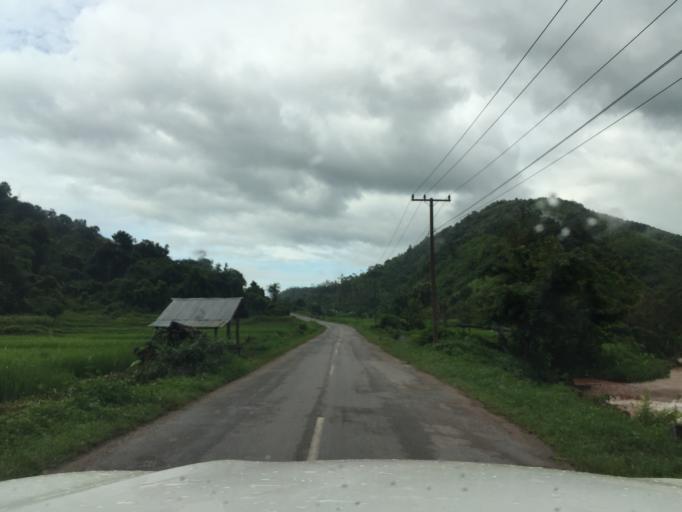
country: LA
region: Oudomxai
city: Muang La
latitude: 20.8197
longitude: 102.0940
